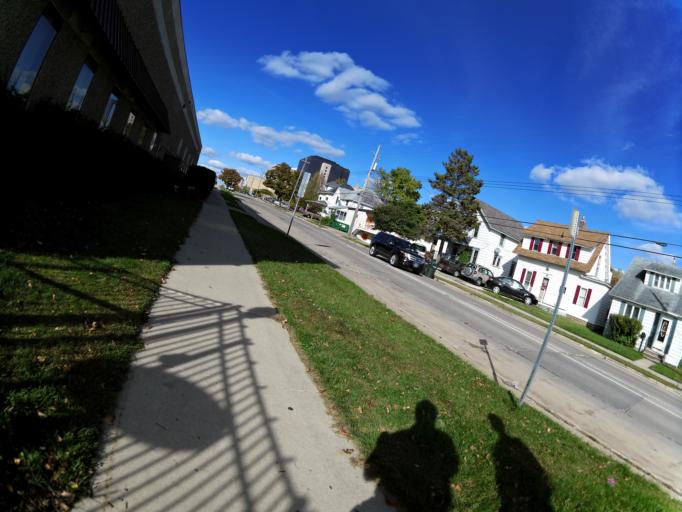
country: US
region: Minnesota
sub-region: Olmsted County
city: Rochester
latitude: 44.0173
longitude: -92.4683
